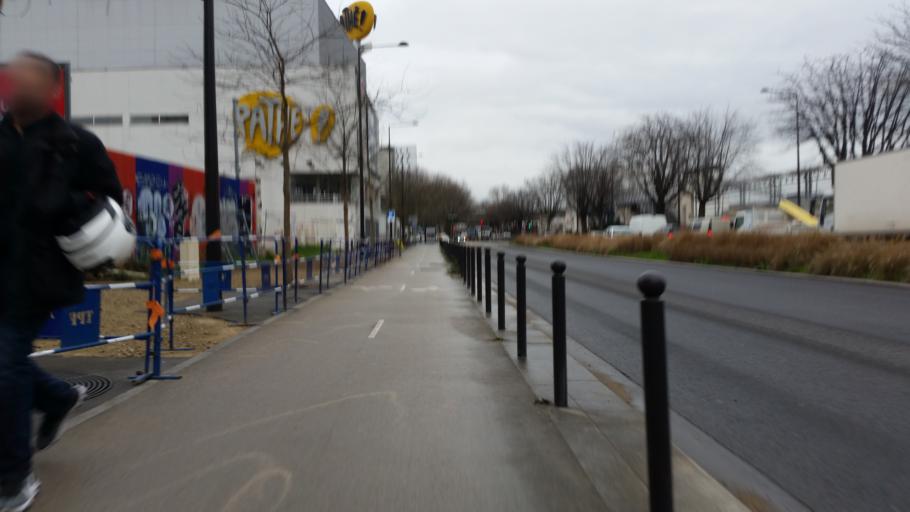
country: FR
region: Ile-de-France
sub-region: Departement du Val-de-Marne
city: Ivry-sur-Seine
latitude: 48.8241
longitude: 2.3901
